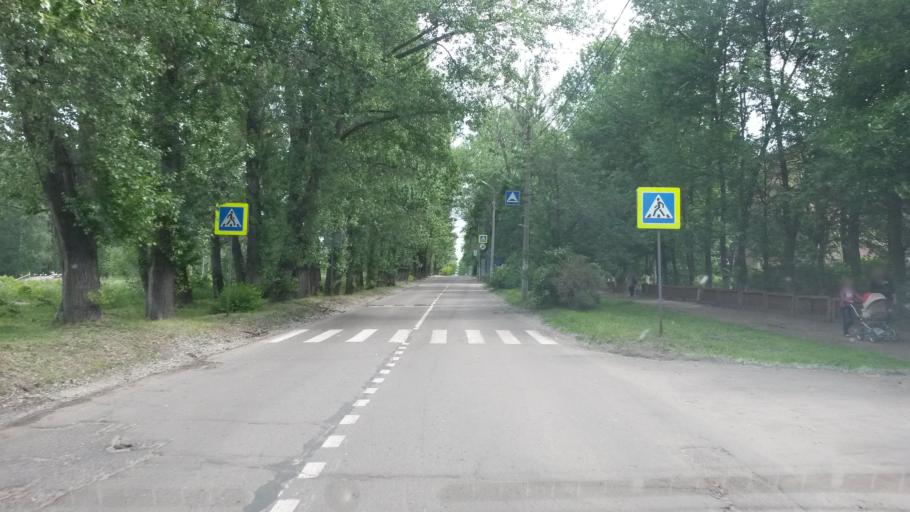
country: RU
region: Jaroslavl
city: Yaroslavl
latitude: 57.5888
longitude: 39.8338
